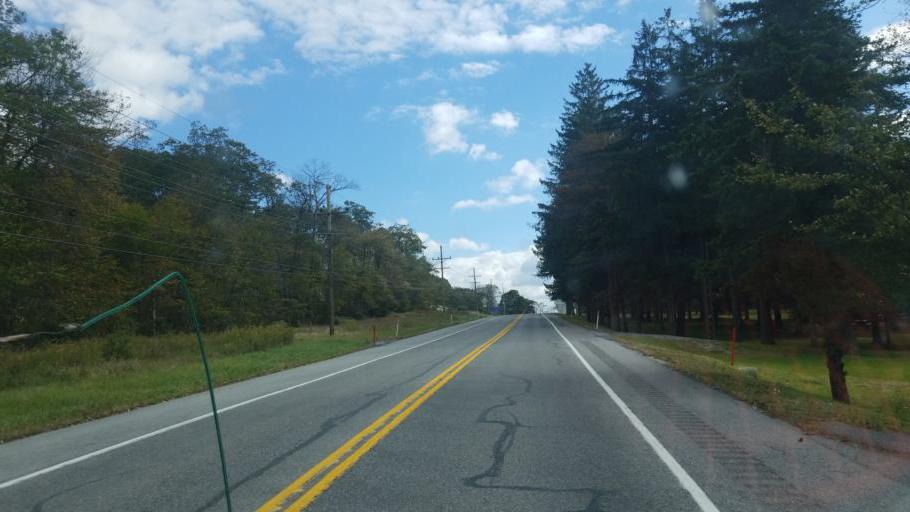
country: US
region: Pennsylvania
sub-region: Fulton County
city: McConnellsburg
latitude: 40.0170
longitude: -78.1537
